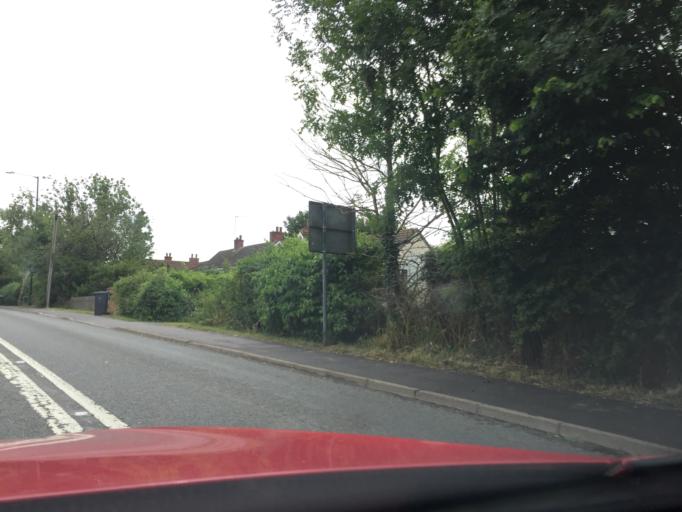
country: GB
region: England
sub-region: Warwickshire
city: Southam
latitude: 52.2596
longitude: -1.3891
